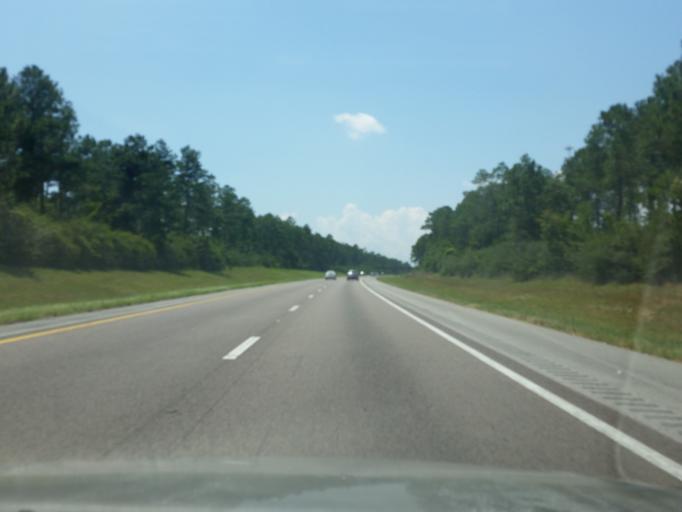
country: US
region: Florida
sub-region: Escambia County
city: Cantonment
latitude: 30.5781
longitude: -87.4692
